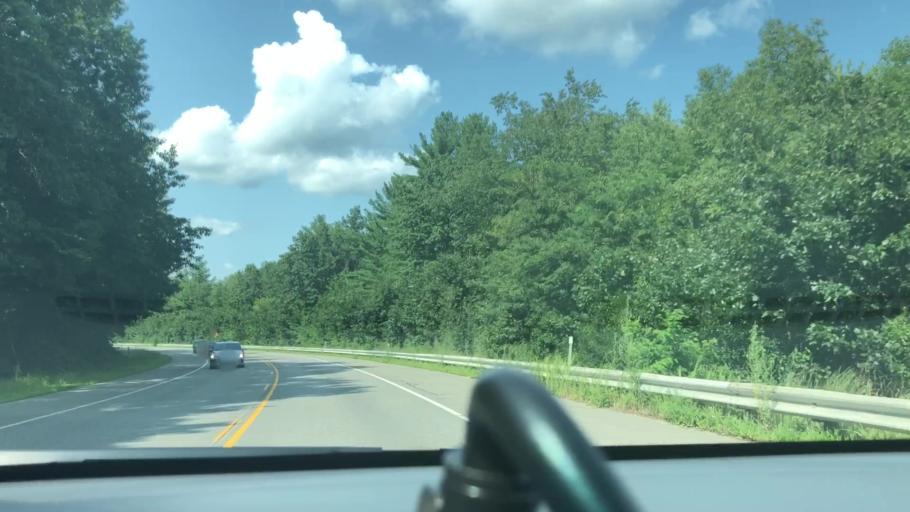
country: US
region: New Hampshire
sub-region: Hillsborough County
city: Pinardville
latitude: 43.0000
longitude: -71.5244
